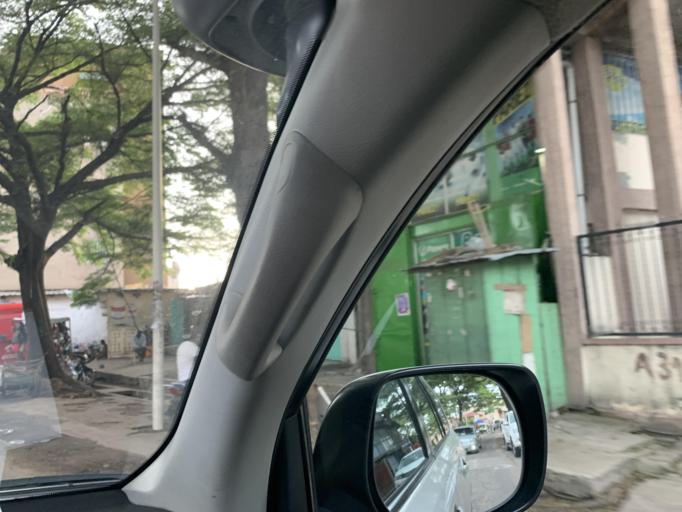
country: CG
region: Brazzaville
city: Brazzaville
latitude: -4.2624
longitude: 15.2895
